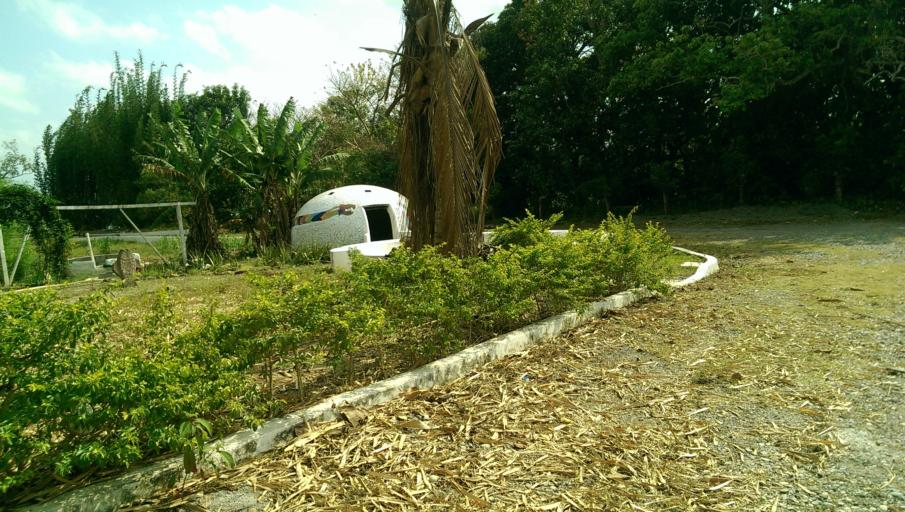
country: MX
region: Veracruz
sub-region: Tuxpan
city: Tierra Blanca
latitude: 20.9143
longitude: -97.4647
